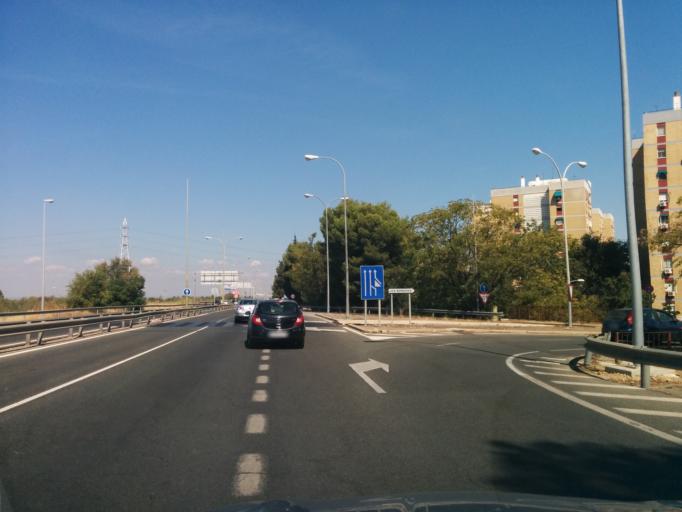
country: ES
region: Andalusia
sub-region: Provincia de Sevilla
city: San Juan de Aznalfarache
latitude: 37.3769
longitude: -6.0145
